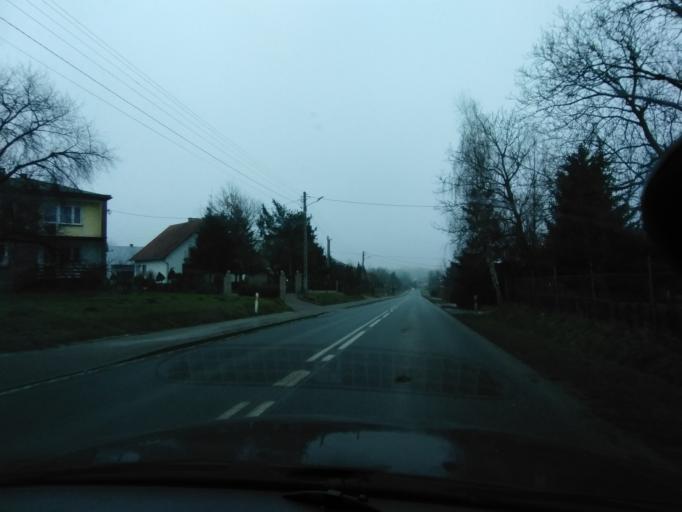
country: PL
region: Subcarpathian Voivodeship
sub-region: Powiat lancucki
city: Sonina
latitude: 50.0587
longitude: 22.2623
